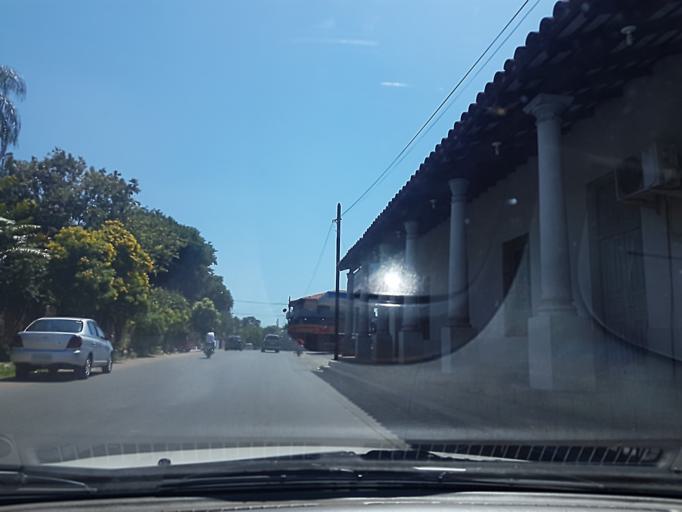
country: PY
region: Central
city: San Lorenzo
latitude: -25.2623
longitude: -57.4895
